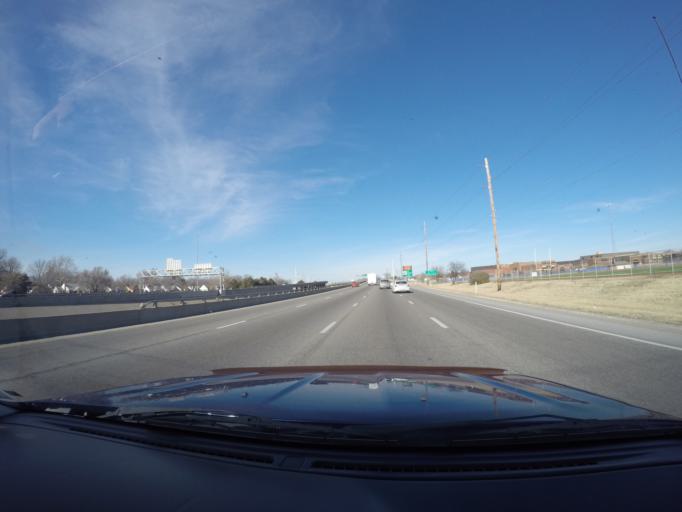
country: US
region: Kansas
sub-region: Sedgwick County
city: Wichita
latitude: 37.6823
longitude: -97.3123
